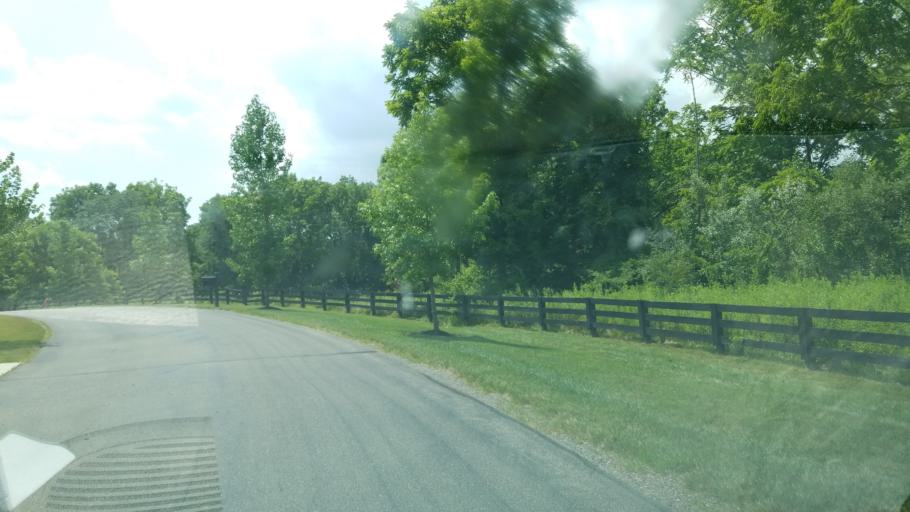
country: US
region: Ohio
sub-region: Delaware County
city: Lewis Center
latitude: 40.2143
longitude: -83.0559
